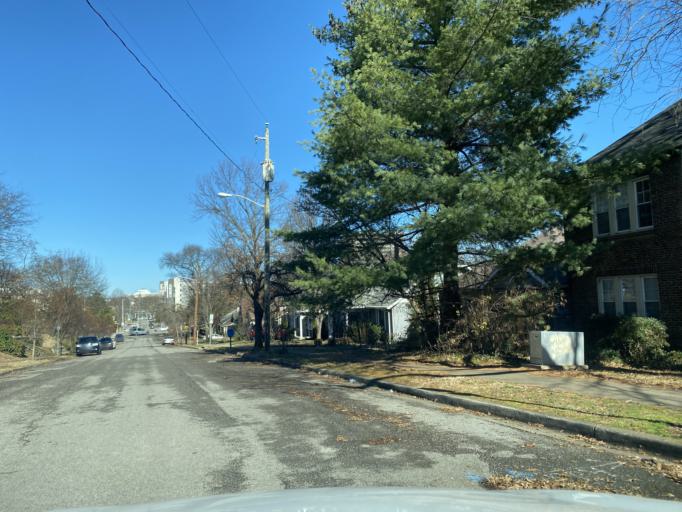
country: US
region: Tennessee
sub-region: Davidson County
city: Nashville
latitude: 36.1332
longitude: -86.8000
